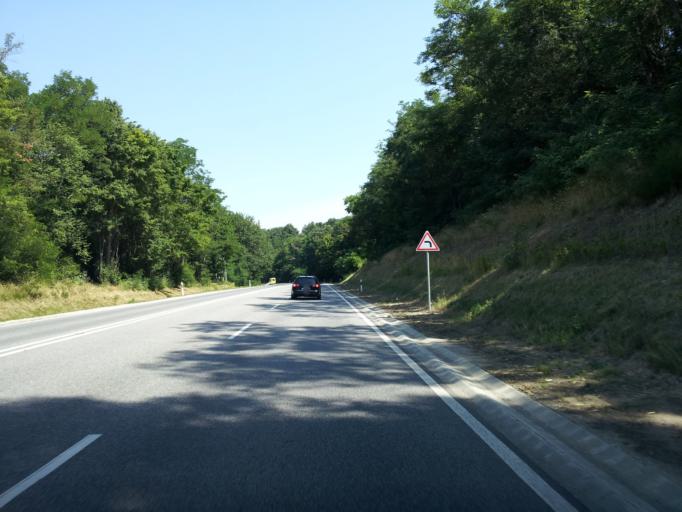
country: HU
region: Zala
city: Pacsa
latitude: 46.8247
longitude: 17.0533
